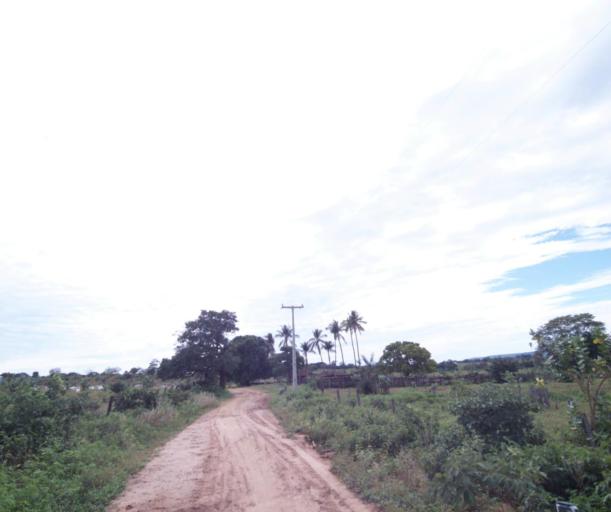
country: BR
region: Bahia
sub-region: Carinhanha
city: Carinhanha
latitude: -14.2402
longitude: -44.3935
